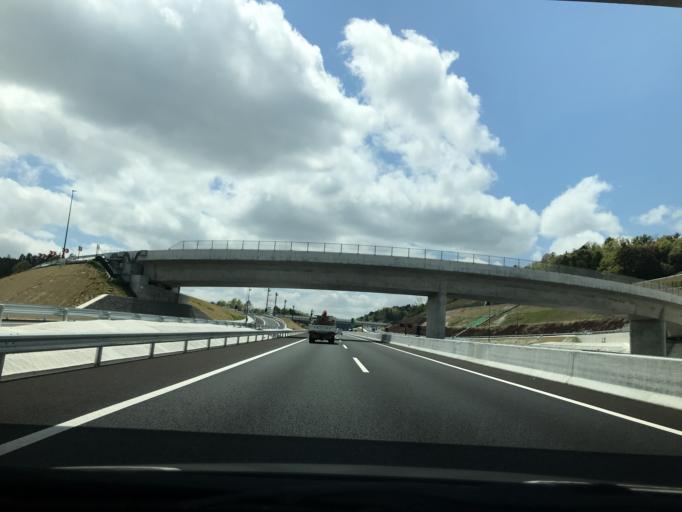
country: JP
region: Osaka
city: Ibaraki
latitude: 34.8849
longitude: 135.5354
